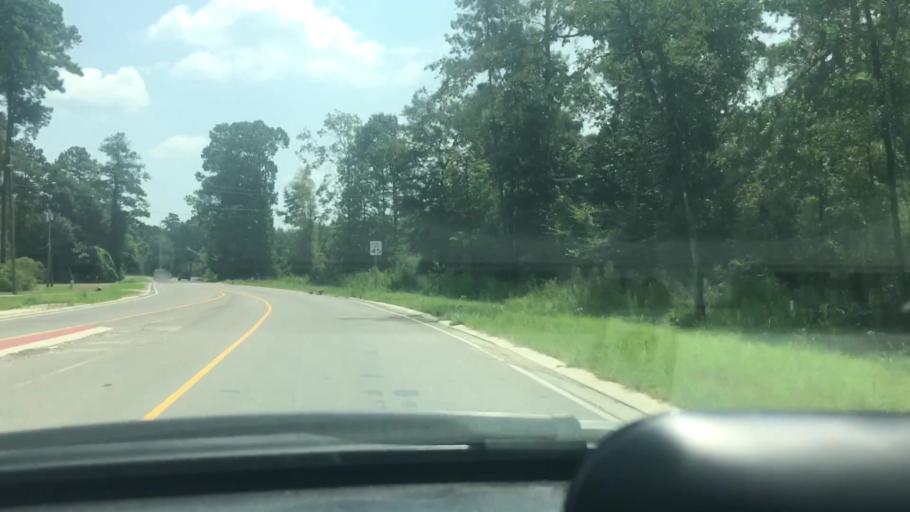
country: US
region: Louisiana
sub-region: Livingston Parish
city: Denham Springs
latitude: 30.4830
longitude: -90.9256
